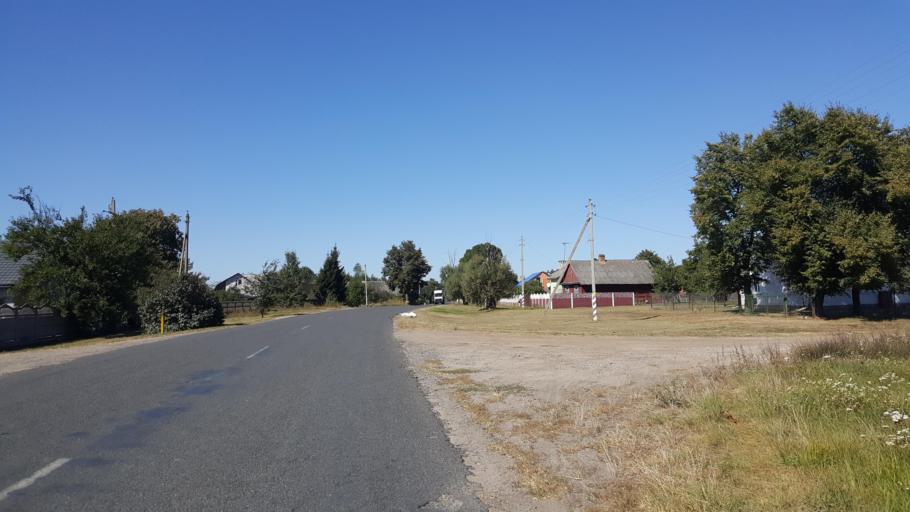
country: PL
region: Lublin Voivodeship
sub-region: Powiat bialski
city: Terespol
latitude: 52.2131
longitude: 23.5144
